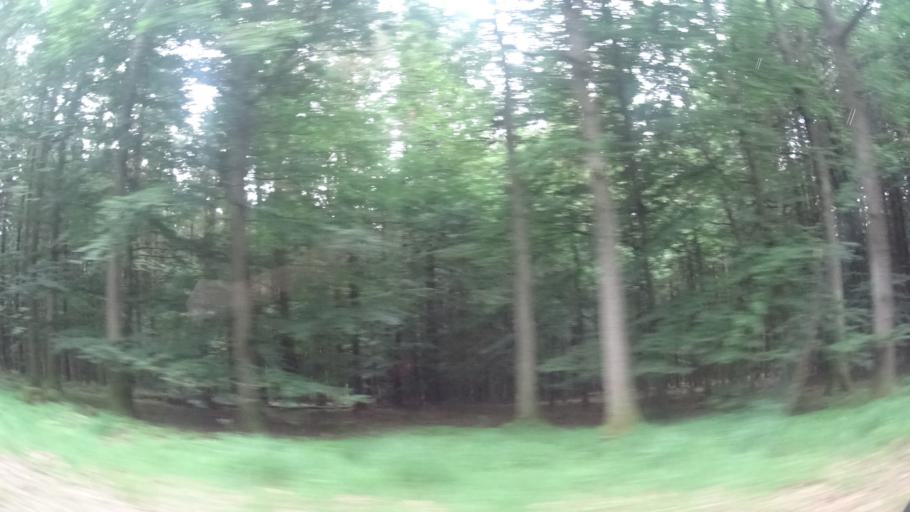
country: DE
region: Hesse
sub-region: Regierungsbezirk Darmstadt
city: Bad Orb
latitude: 50.1893
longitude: 9.4188
